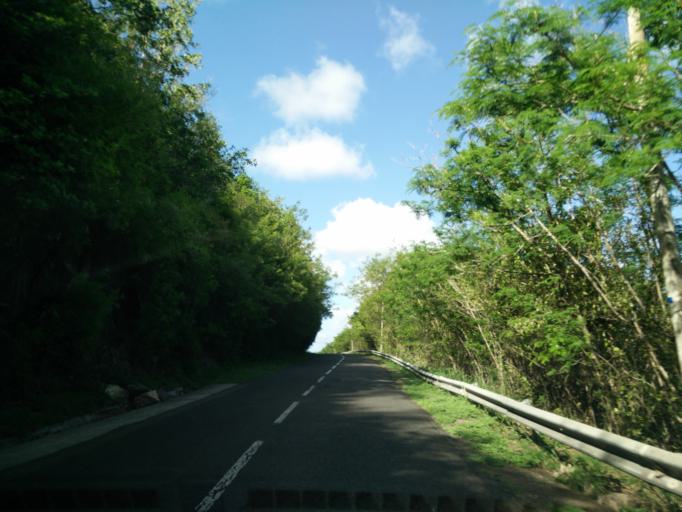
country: MQ
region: Martinique
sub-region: Martinique
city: Les Trois-Ilets
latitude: 14.4571
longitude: -61.0514
